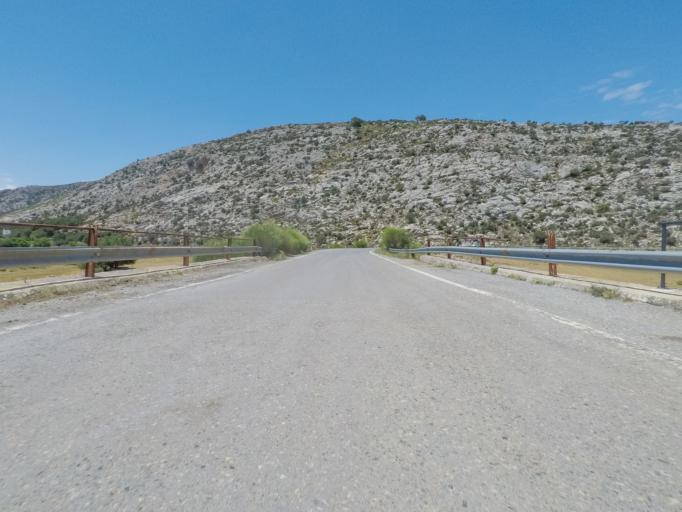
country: GR
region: Crete
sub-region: Nomos Irakleiou
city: Mokhos
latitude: 35.1923
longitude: 25.4322
